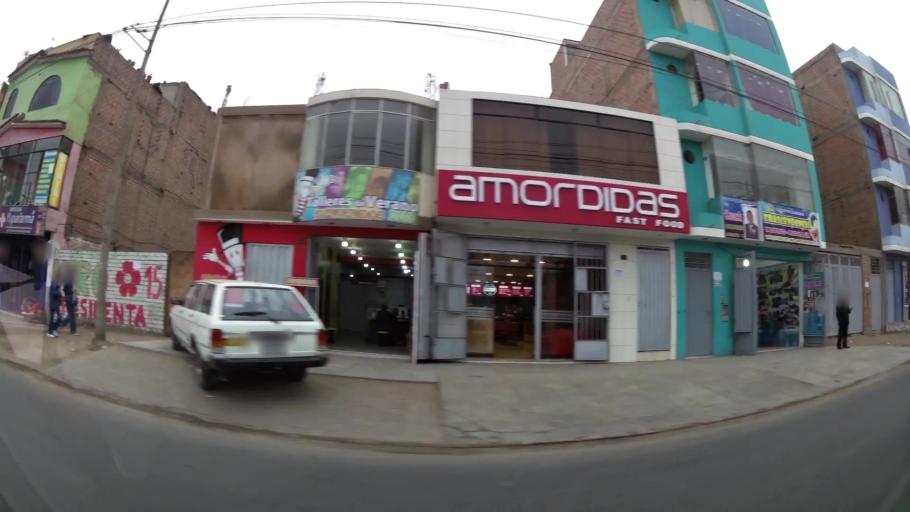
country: PE
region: Lima
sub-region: Lima
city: Urb. Santo Domingo
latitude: -11.8874
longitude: -77.0360
